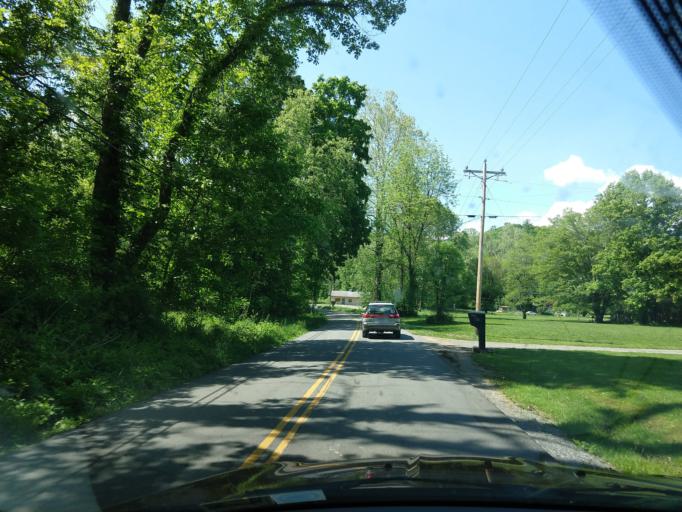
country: US
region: Virginia
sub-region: City of Covington
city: Fairlawn
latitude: 37.6910
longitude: -79.8889
